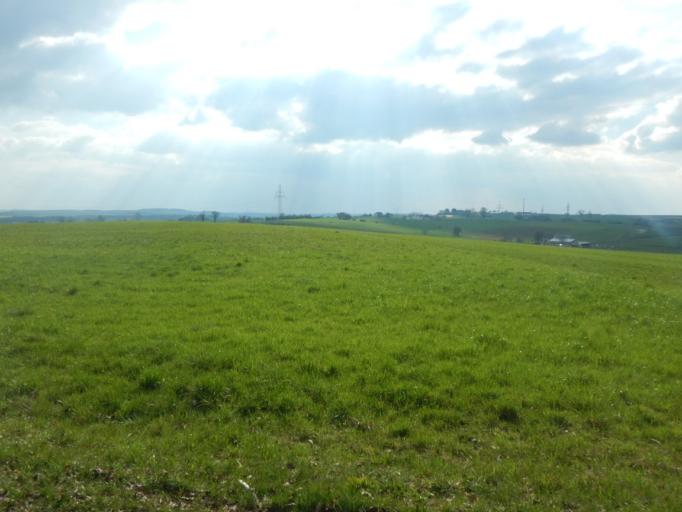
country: LU
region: Grevenmacher
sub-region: Canton d'Echternach
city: Waldbillig
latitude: 49.8081
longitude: 6.2725
